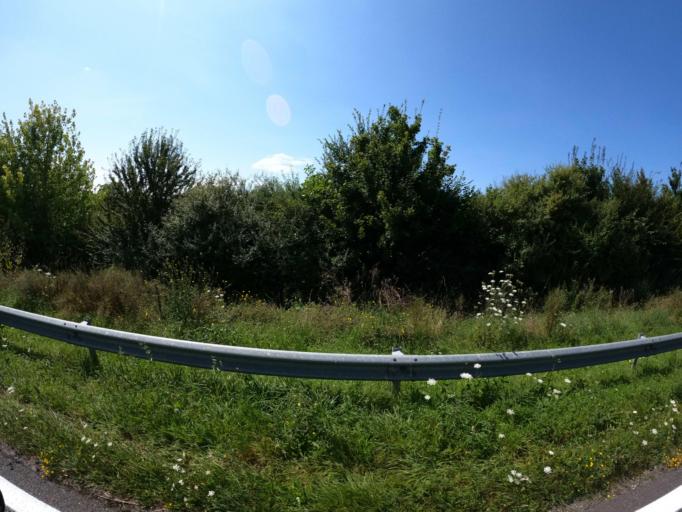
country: FR
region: Poitou-Charentes
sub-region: Departement de la Vienne
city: Availles-Limouzine
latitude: 46.1122
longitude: 0.5656
